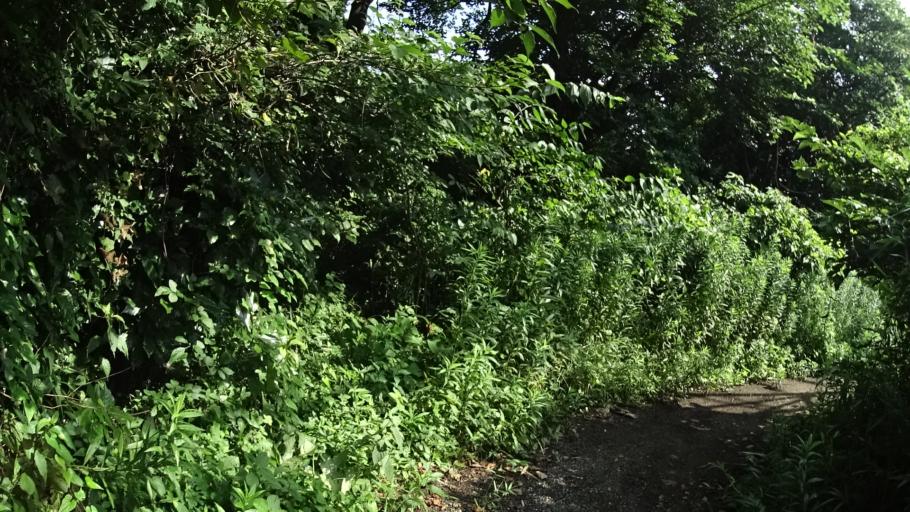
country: JP
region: Kanagawa
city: Zushi
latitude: 35.3127
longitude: 139.6074
